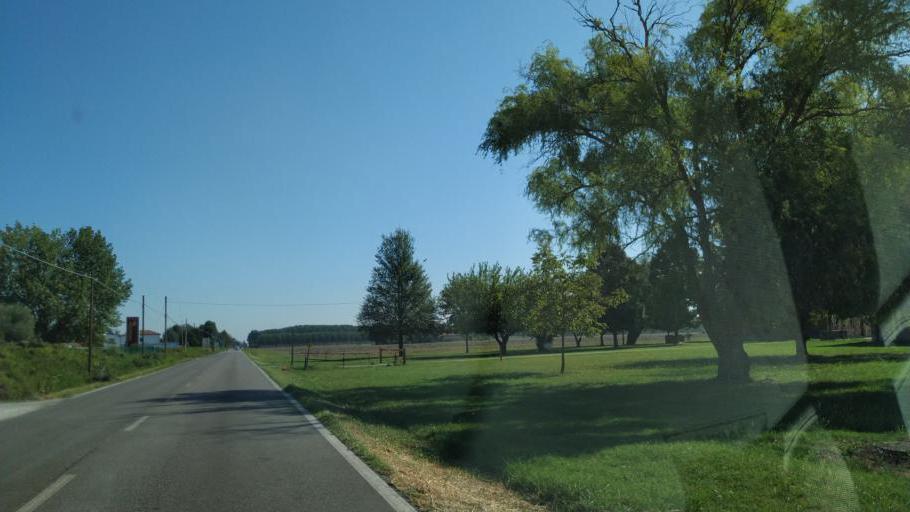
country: IT
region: Emilia-Romagna
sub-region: Provincia di Ferrara
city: Mirabello
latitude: 44.8112
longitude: 11.4352
